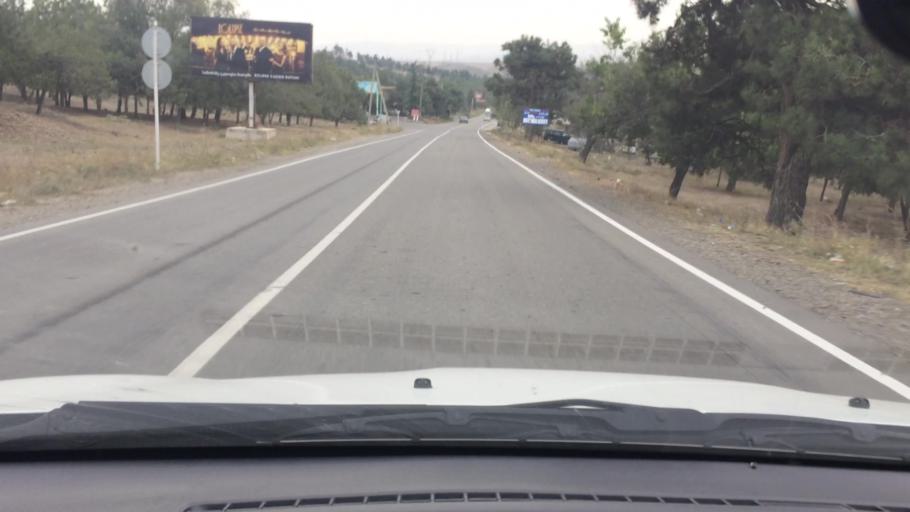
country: GE
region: Kvemo Kartli
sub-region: Gardabani
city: Gardabani
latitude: 41.3426
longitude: 45.0684
